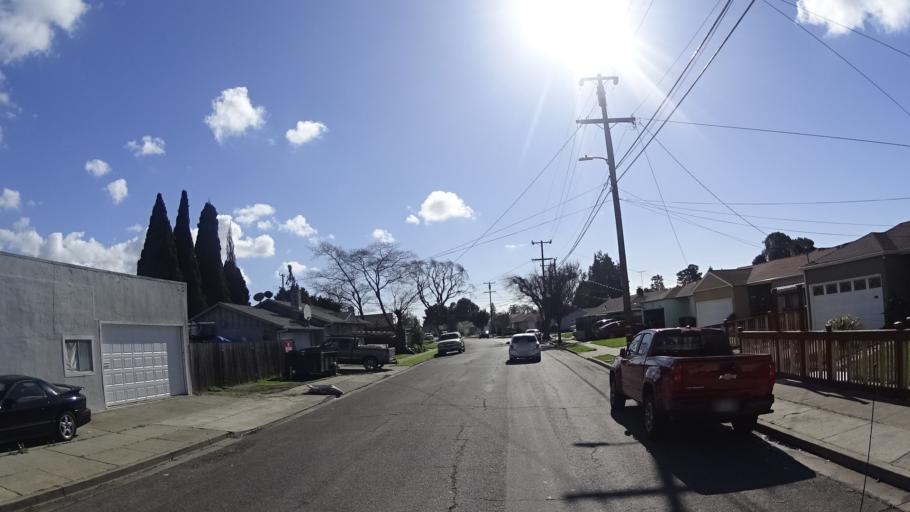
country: US
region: California
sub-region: Alameda County
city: Cherryland
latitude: 37.6607
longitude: -122.1066
